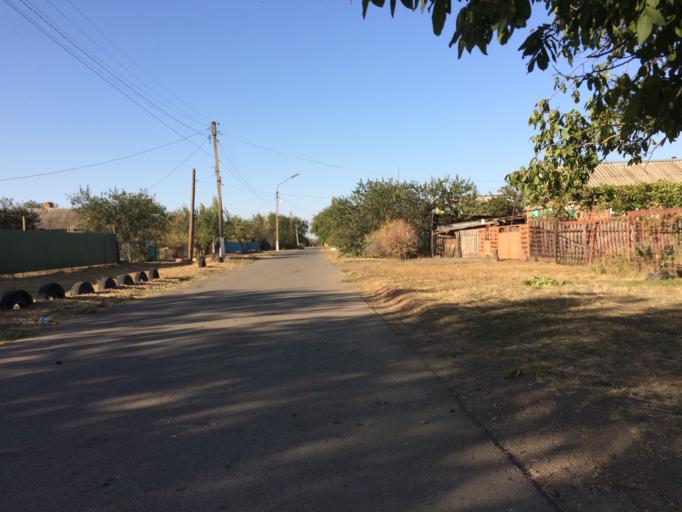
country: RU
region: Rostov
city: Tselina
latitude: 46.5173
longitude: 41.1860
